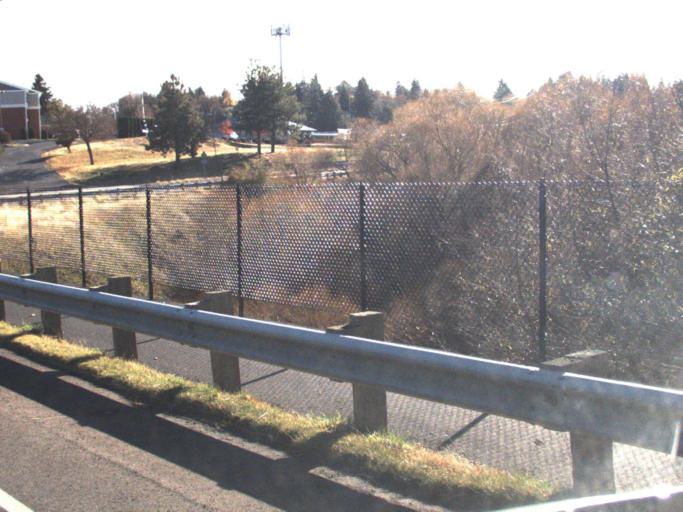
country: US
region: Washington
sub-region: Whitman County
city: Pullman
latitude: 46.7336
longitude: -117.1947
